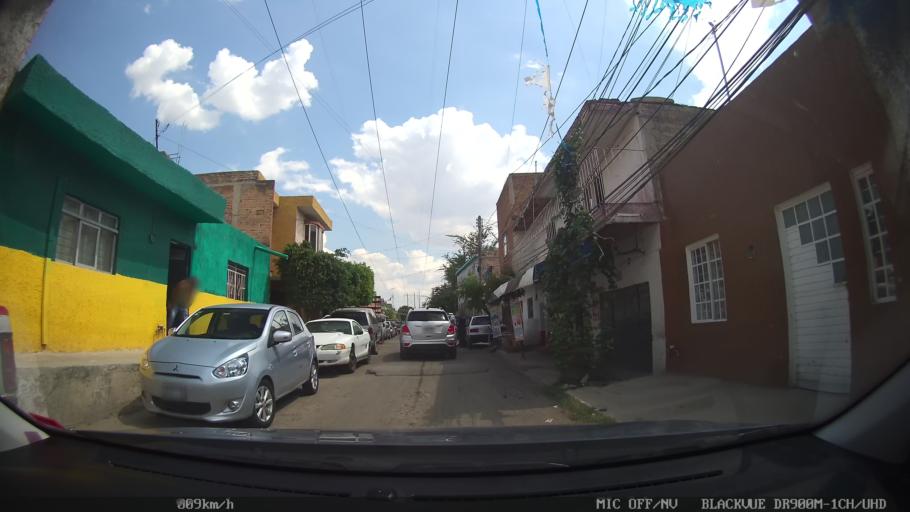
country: MX
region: Jalisco
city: Tonala
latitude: 20.6241
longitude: -103.2640
